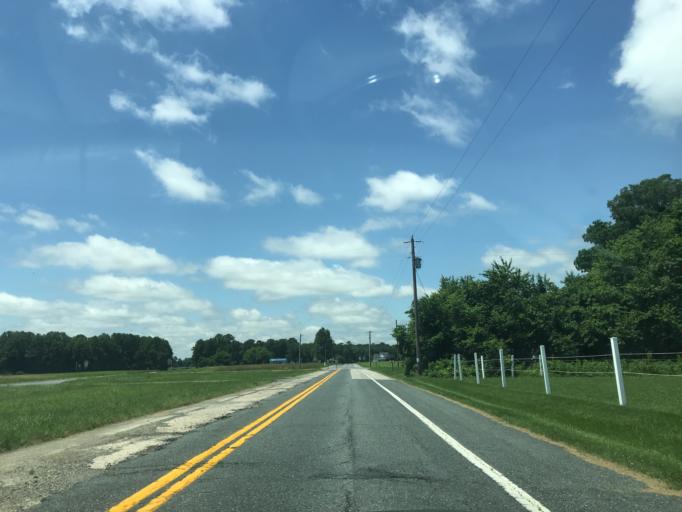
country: US
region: Maryland
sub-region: Caroline County
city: Federalsburg
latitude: 38.6994
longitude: -75.7359
